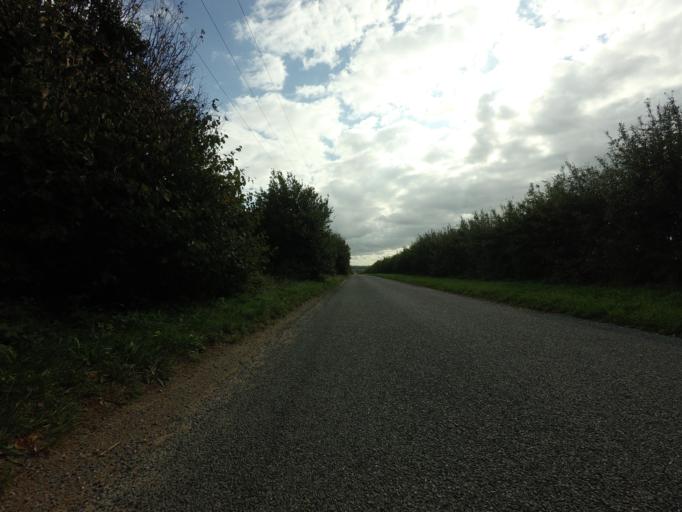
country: GB
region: England
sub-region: Norfolk
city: Heacham
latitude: 52.9173
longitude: 0.5425
